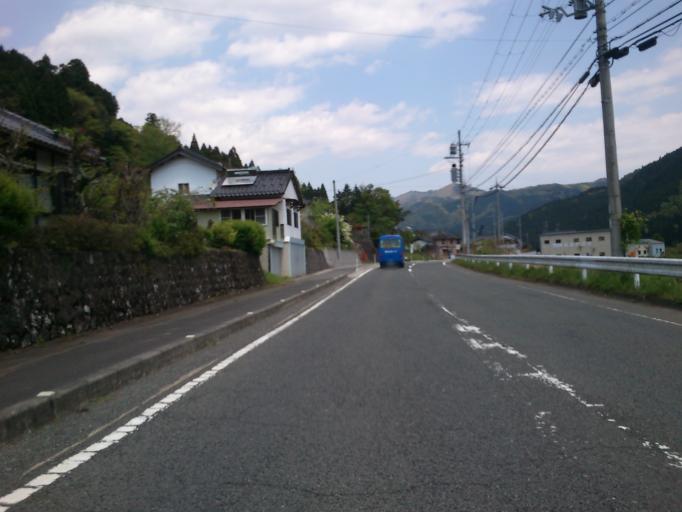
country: JP
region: Kyoto
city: Fukuchiyama
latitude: 35.3445
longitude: 134.9391
